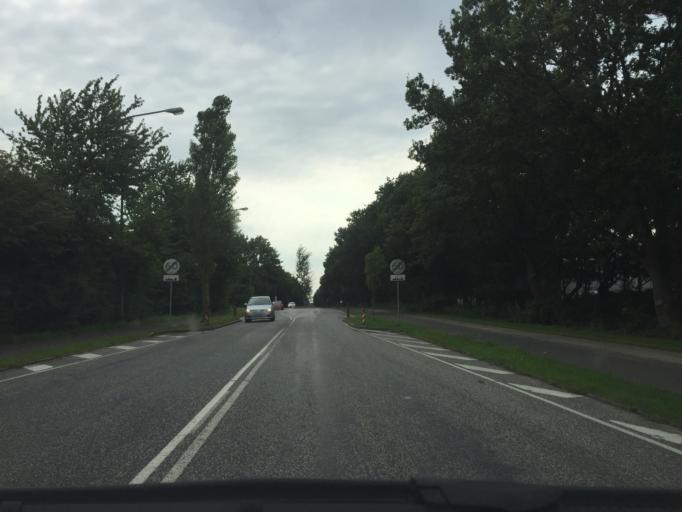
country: DK
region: Capital Region
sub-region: Lyngby-Tarbaek Kommune
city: Kongens Lyngby
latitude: 55.7892
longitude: 12.5280
